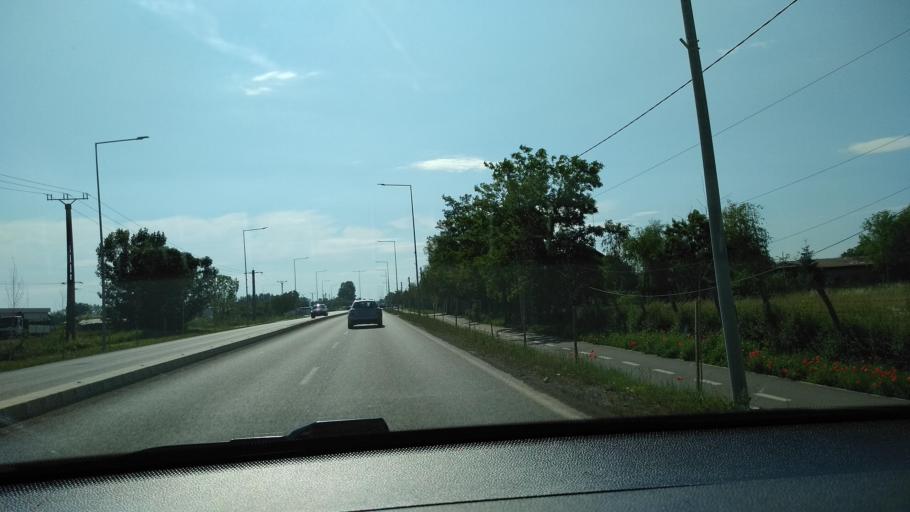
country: RO
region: Timis
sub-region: Comuna Mosnita Noua
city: Mosnita Noua
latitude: 45.7216
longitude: 21.3072
